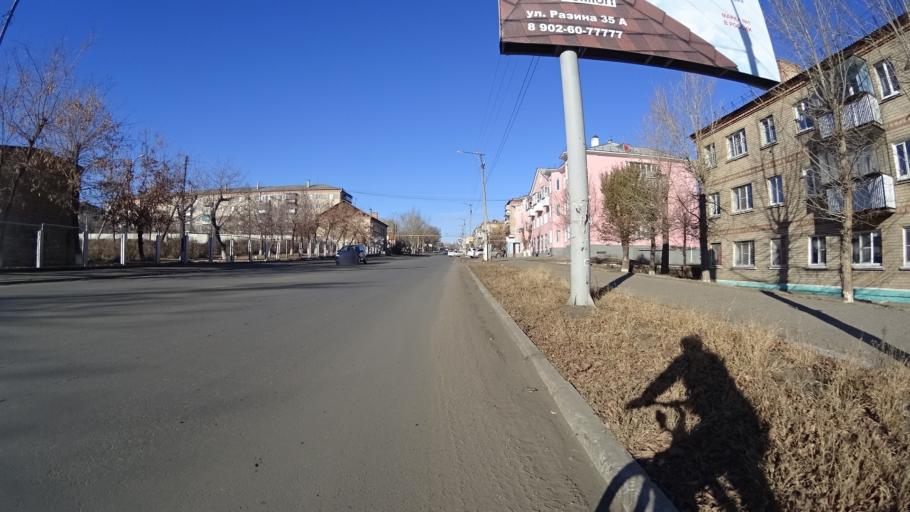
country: RU
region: Chelyabinsk
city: Troitsk
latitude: 54.0779
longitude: 61.5385
